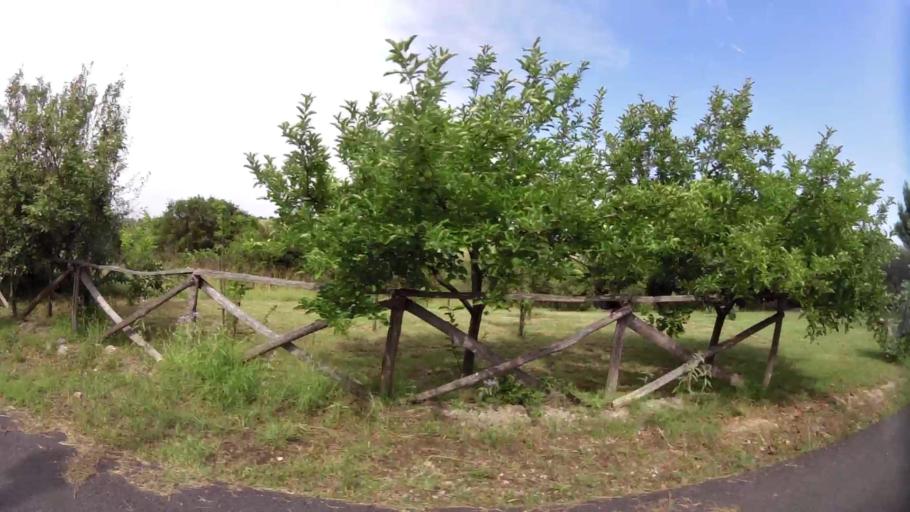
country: GR
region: Central Macedonia
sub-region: Nomos Thessalonikis
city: Panorama
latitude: 40.5751
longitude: 23.0058
